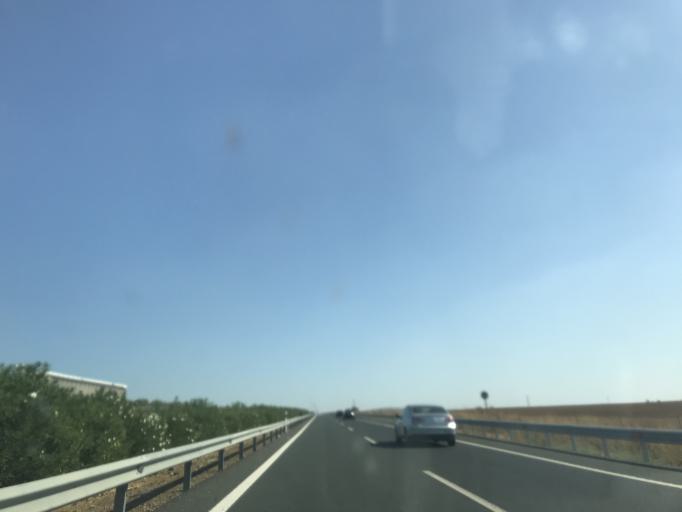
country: ES
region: Andalusia
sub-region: Provincia de Sevilla
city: Mairena del Alcor
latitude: 37.3201
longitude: -5.7671
